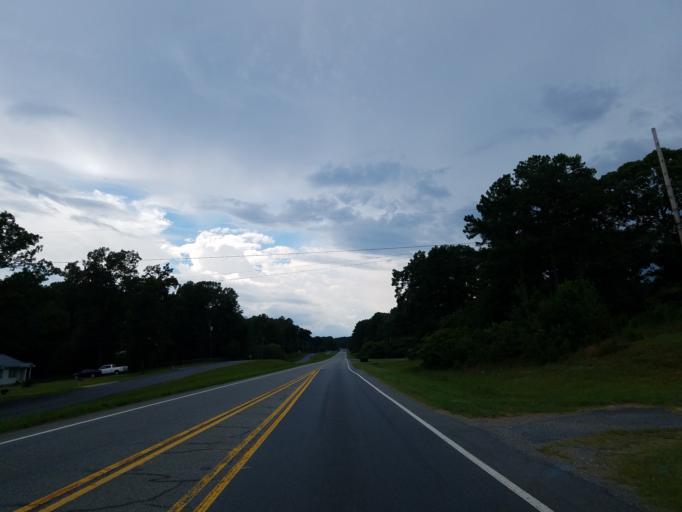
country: US
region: Georgia
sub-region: Bartow County
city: Adairsville
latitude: 34.3007
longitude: -84.8815
